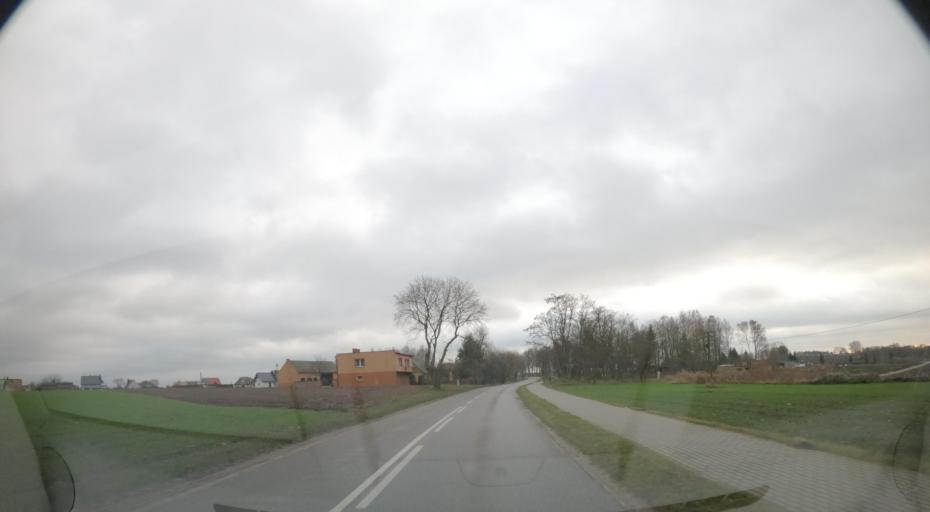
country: PL
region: Greater Poland Voivodeship
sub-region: Powiat pilski
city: Lobzenica
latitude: 53.2578
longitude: 17.2622
